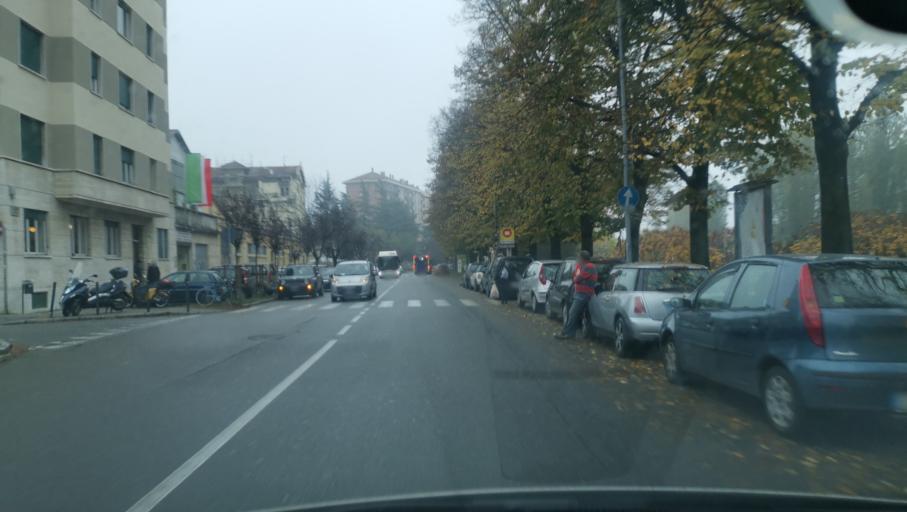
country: IT
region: Piedmont
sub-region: Provincia di Torino
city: Turin
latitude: 45.0743
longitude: 7.6978
